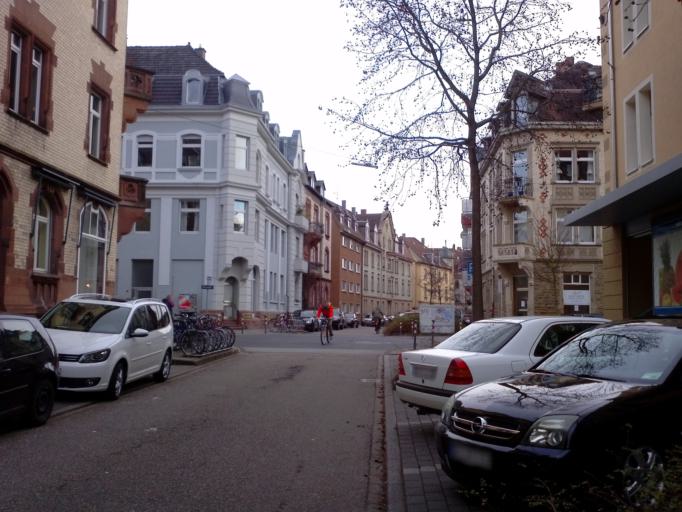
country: DE
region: Baden-Wuerttemberg
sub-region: Karlsruhe Region
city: Karlsruhe
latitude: 49.0024
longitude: 8.3891
